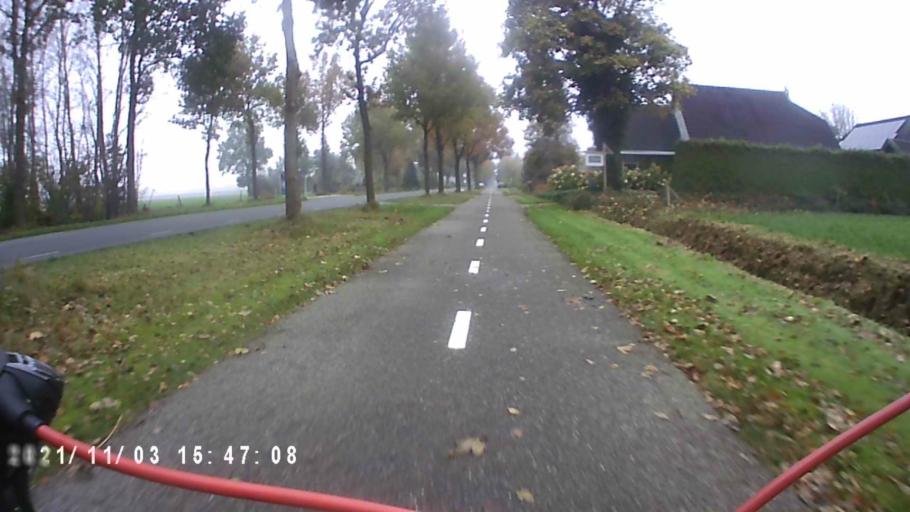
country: NL
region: Groningen
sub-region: Gemeente Leek
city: Leek
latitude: 53.0916
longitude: 6.3402
